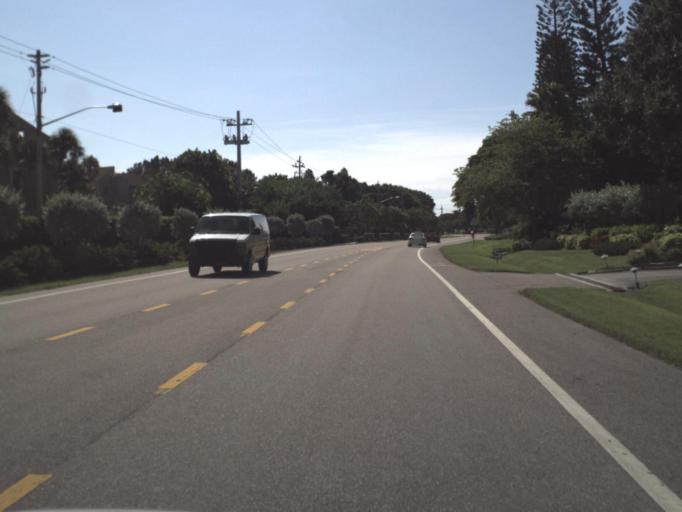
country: US
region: Florida
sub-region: Manatee County
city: Longboat Key
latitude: 27.3991
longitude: -82.6477
